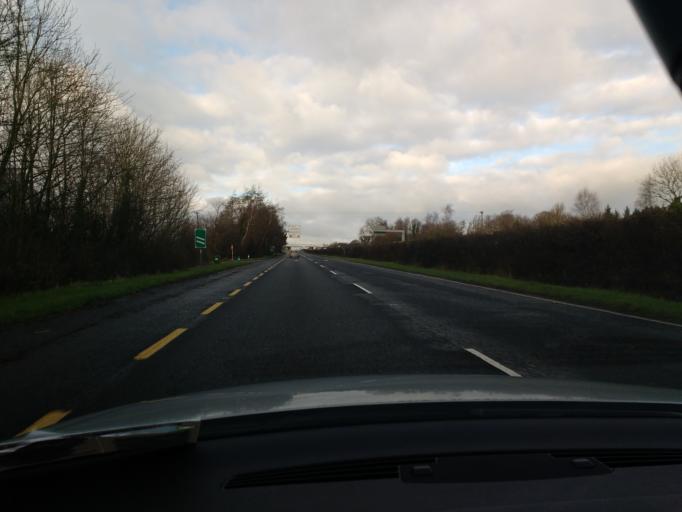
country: IE
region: Munster
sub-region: An Clar
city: Shannon
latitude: 52.7036
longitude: -8.8337
